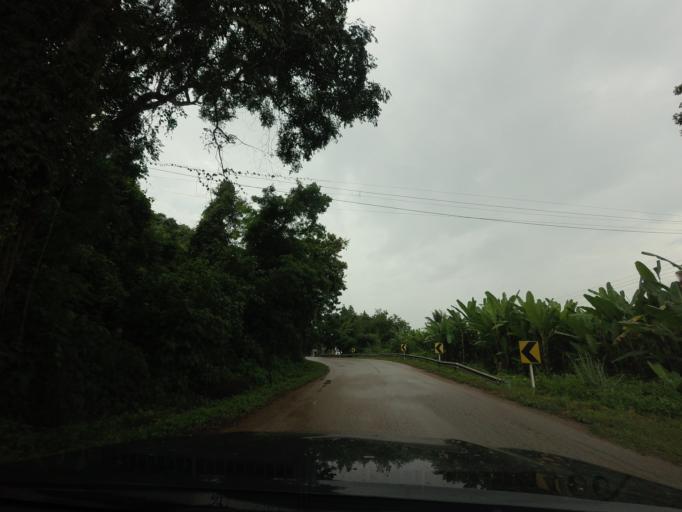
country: TH
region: Loei
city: Pak Chom
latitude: 18.1104
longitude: 101.9826
